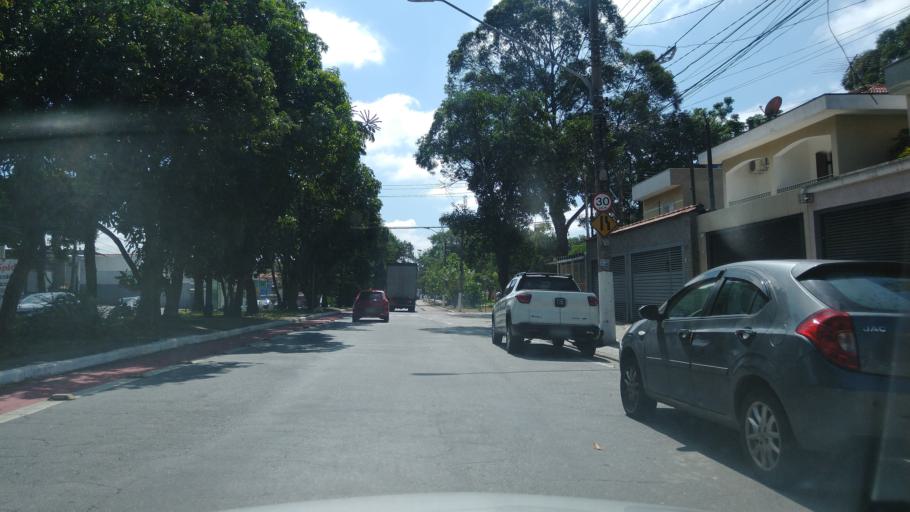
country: BR
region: Sao Paulo
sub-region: Guarulhos
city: Guarulhos
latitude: -23.4946
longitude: -46.5713
